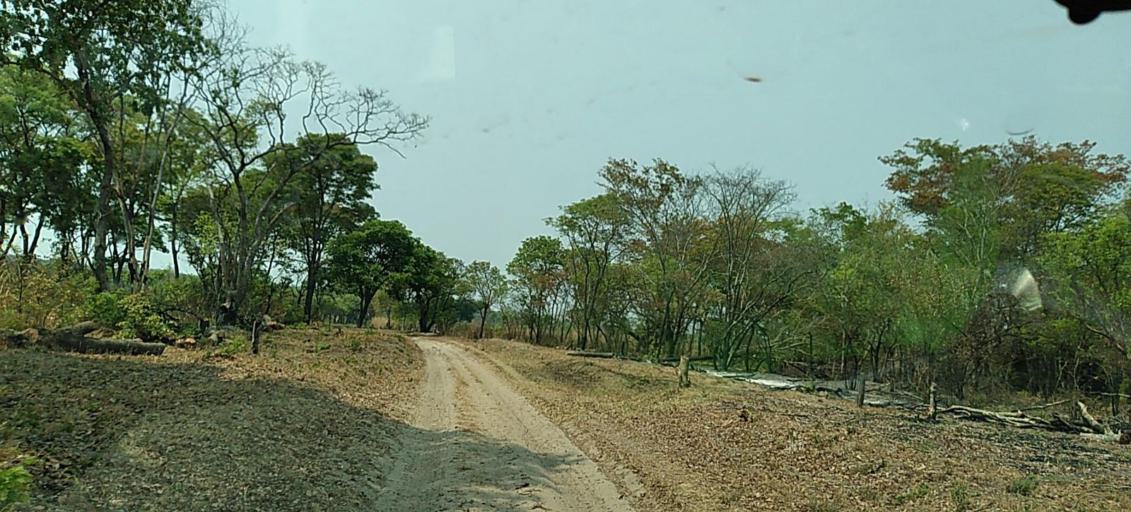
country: ZM
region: Western
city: Lukulu
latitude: -13.9648
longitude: 23.2263
